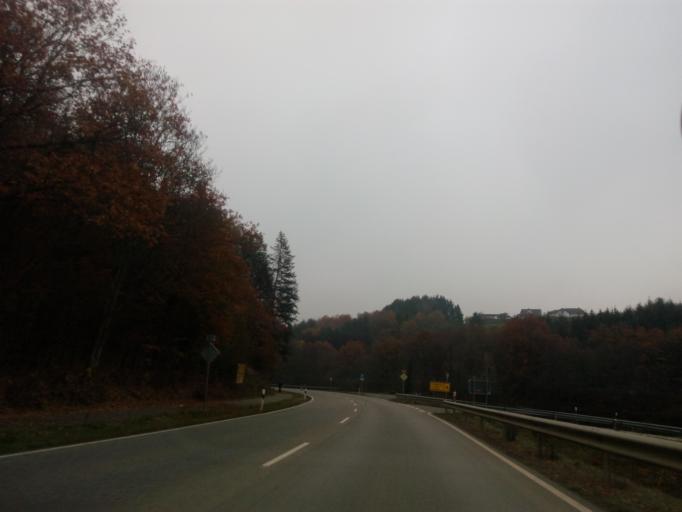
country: DE
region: Rheinland-Pfalz
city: Grumbach
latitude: 49.6527
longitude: 7.5730
